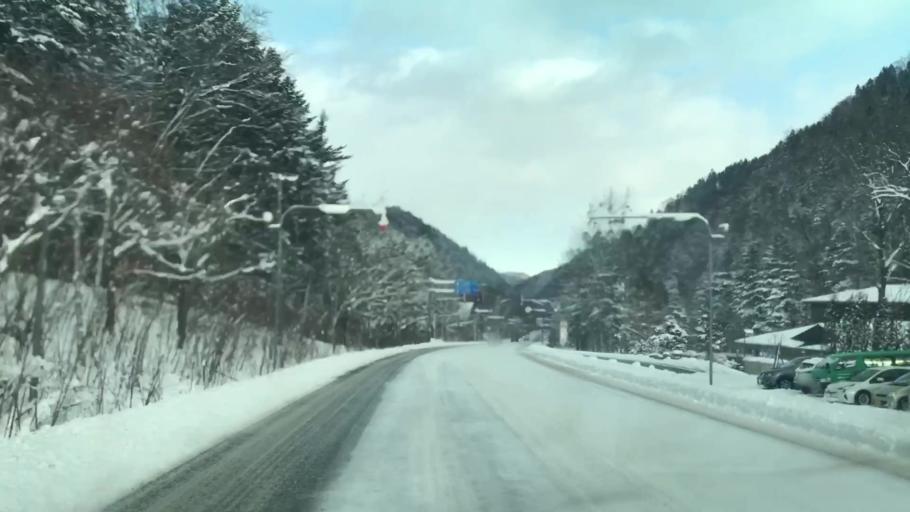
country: JP
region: Hokkaido
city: Sapporo
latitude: 42.9418
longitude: 141.1280
